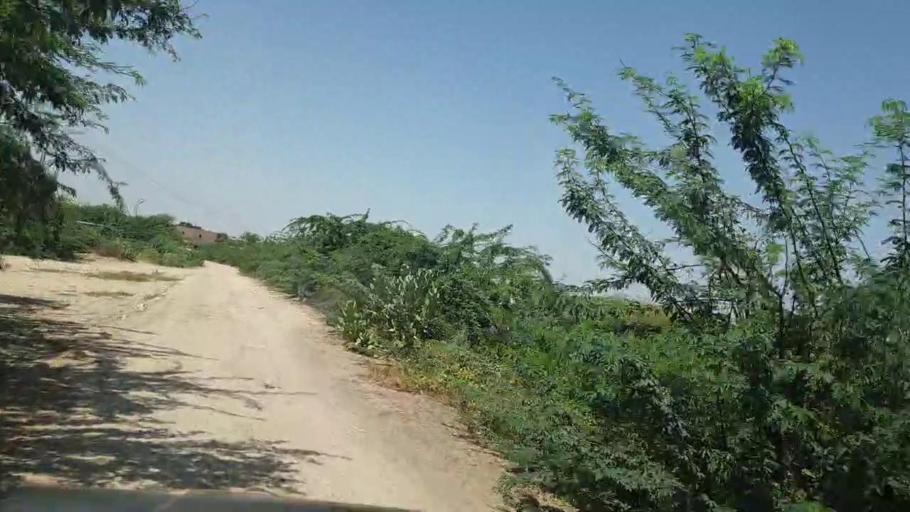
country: PK
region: Sindh
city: Chor
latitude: 25.4100
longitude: 70.3068
